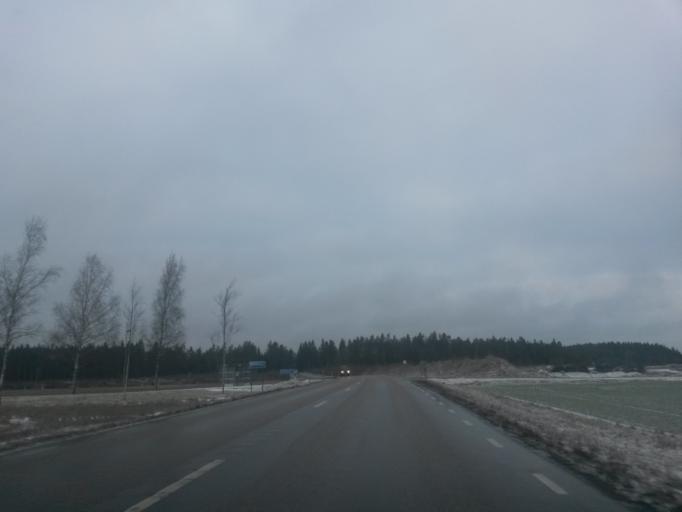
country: SE
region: Vaestra Goetaland
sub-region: Essunga Kommun
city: Nossebro
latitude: 58.1007
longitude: 12.6565
